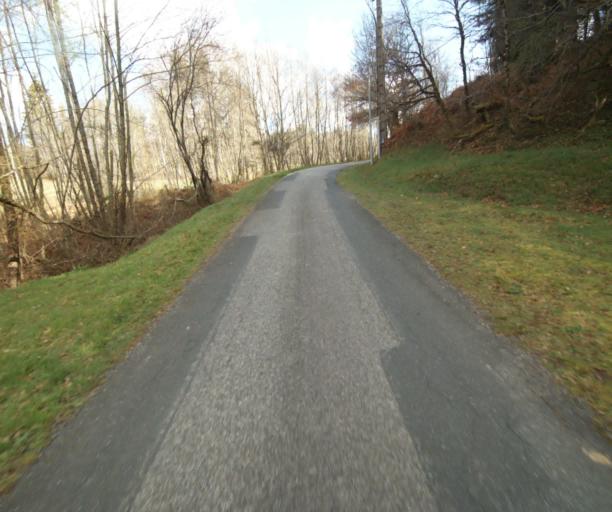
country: FR
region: Limousin
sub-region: Departement de la Correze
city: Laguenne
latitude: 45.2339
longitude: 1.8990
